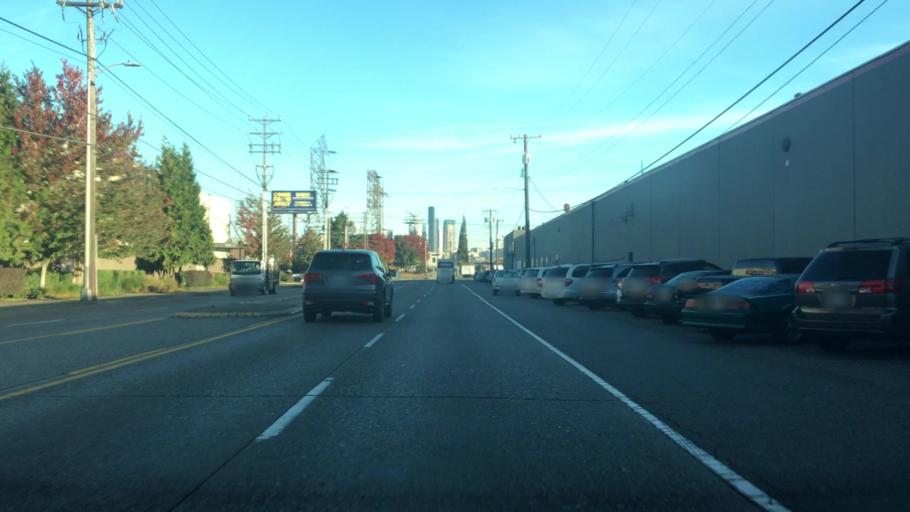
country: US
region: Washington
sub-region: King County
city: Seattle
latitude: 47.5653
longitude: -122.3294
